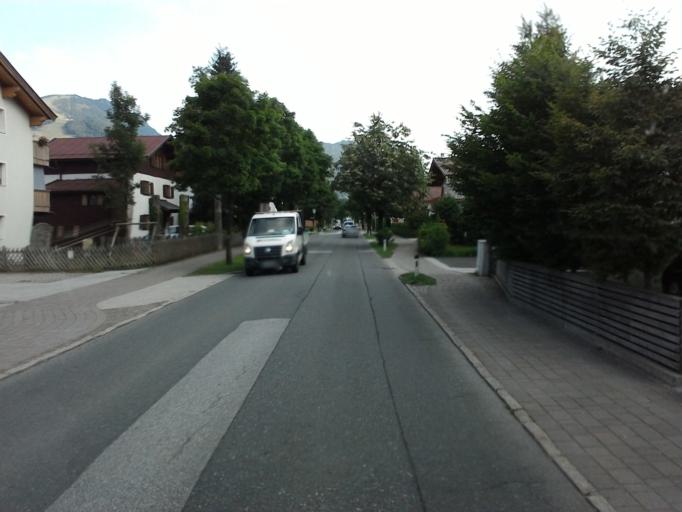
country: AT
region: Tyrol
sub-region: Politischer Bezirk Kitzbuhel
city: Kossen
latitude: 47.6649
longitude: 12.4043
